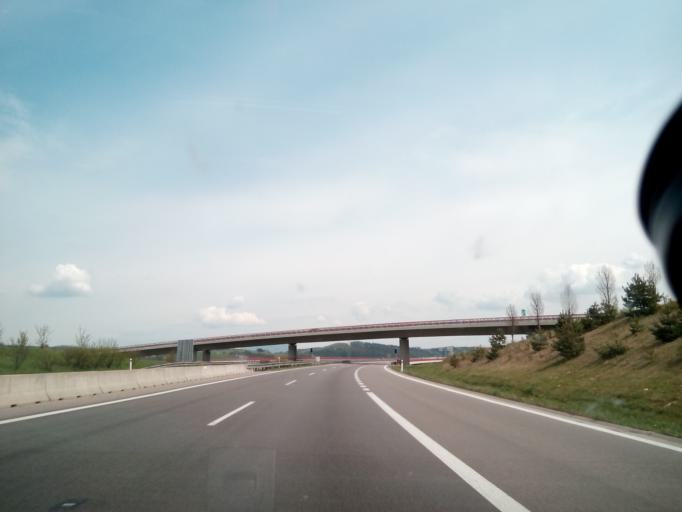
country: SK
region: Nitriansky
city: Puchov
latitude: 49.0626
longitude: 18.3387
